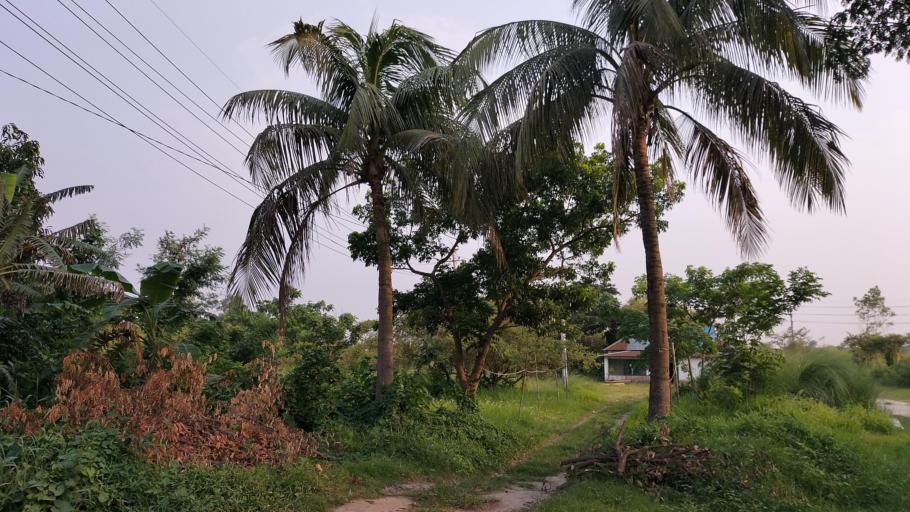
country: BD
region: Dhaka
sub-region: Dhaka
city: Dhaka
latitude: 23.6552
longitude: 90.3410
